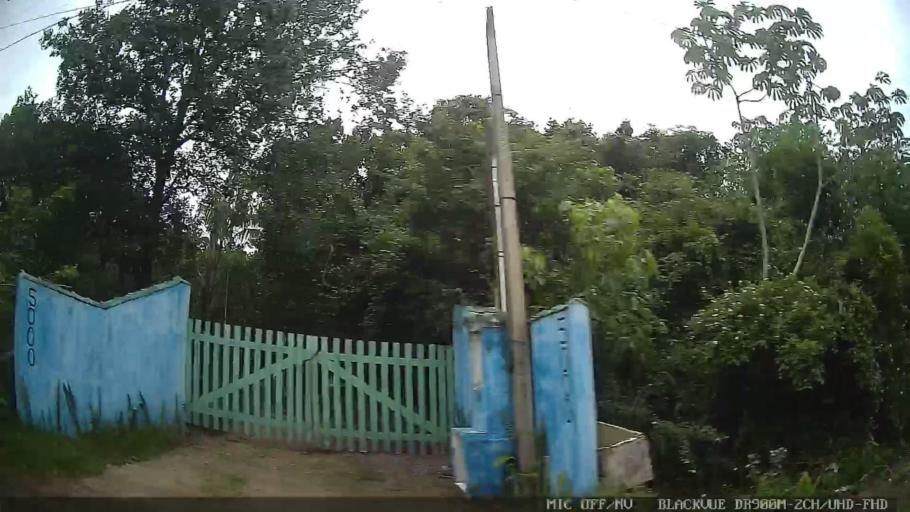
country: BR
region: Sao Paulo
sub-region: Iguape
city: Iguape
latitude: -24.6706
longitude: -47.4443
